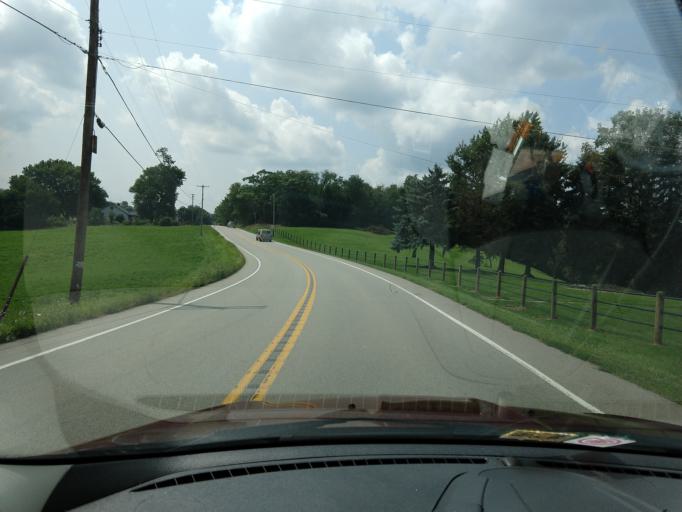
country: US
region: Pennsylvania
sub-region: Washington County
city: McMurray
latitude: 40.1865
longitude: -80.0800
